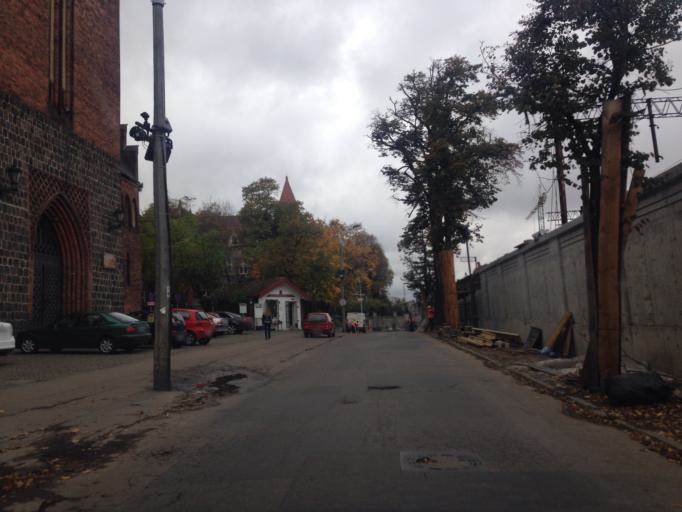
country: PL
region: Pomeranian Voivodeship
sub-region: Gdansk
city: Gdansk
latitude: 54.3800
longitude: 18.6098
